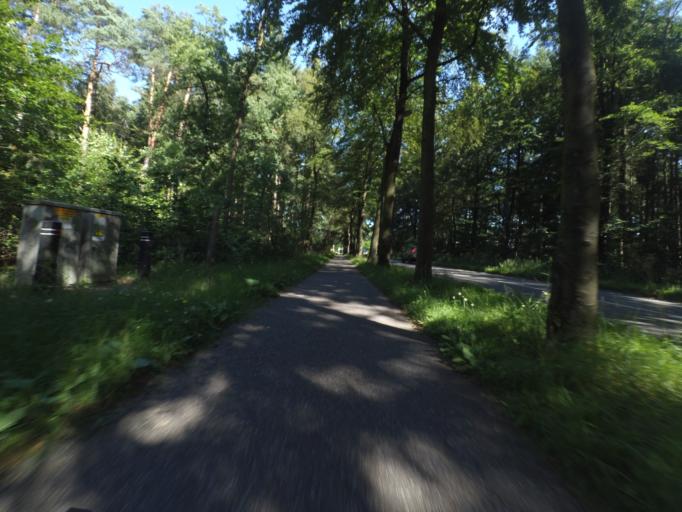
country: NL
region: Utrecht
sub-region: Gemeente Utrechtse Heuvelrug
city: Doorn
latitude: 52.0466
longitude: 5.3252
